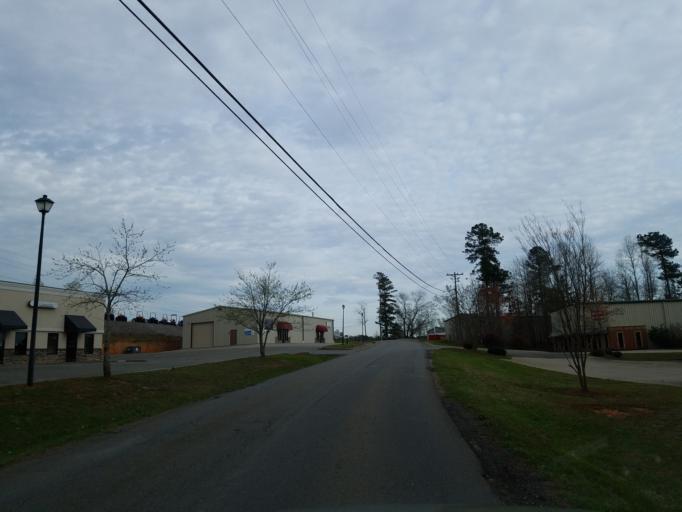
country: US
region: Georgia
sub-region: Pickens County
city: Jasper
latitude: 34.4754
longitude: -84.4587
